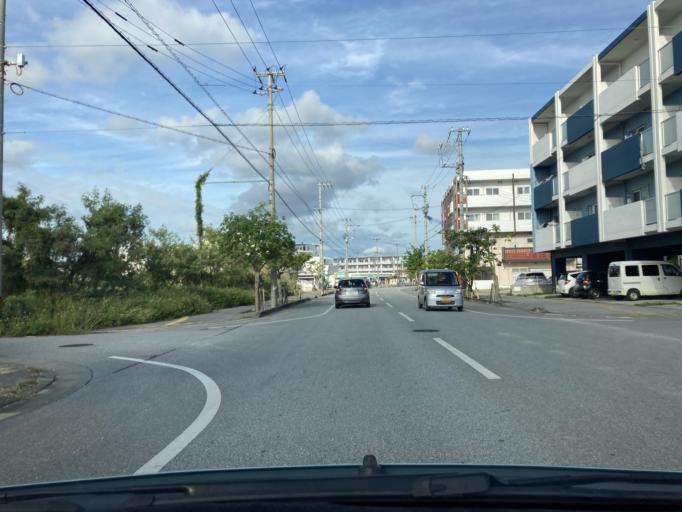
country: JP
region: Okinawa
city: Itoman
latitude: 26.1227
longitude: 127.6741
